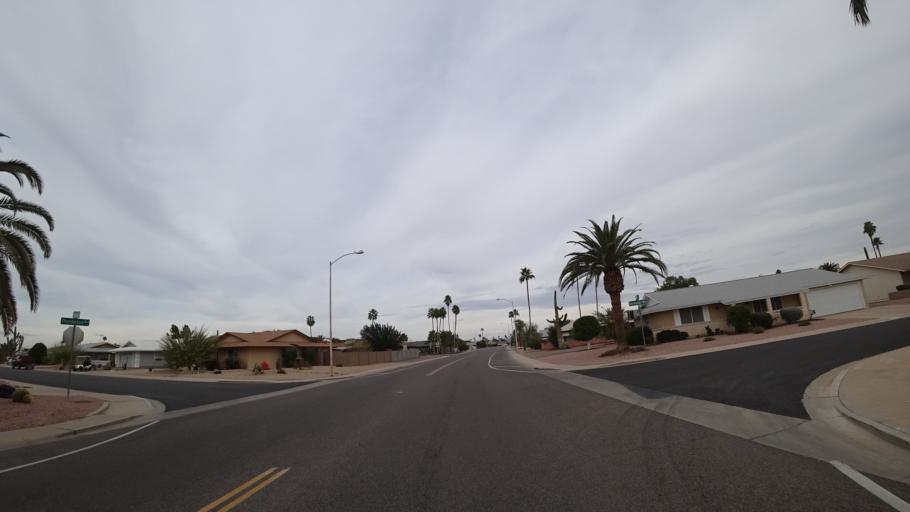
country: US
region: Arizona
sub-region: Maricopa County
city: Youngtown
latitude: 33.6156
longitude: -112.2977
